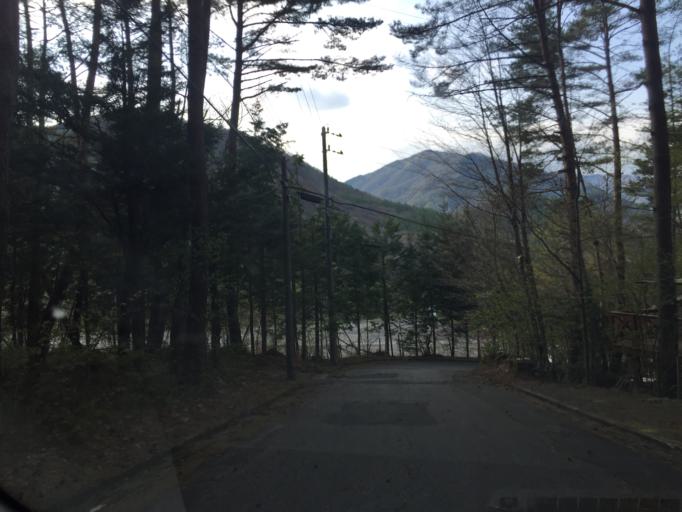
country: JP
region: Gifu
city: Nakatsugawa
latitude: 35.3561
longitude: 137.6729
